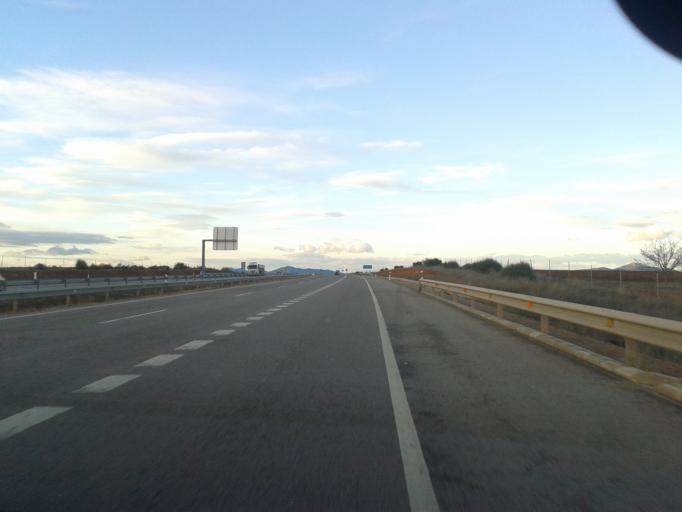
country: ES
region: Aragon
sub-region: Provincia de Zaragoza
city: Lechon
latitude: 41.0542
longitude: -1.2782
